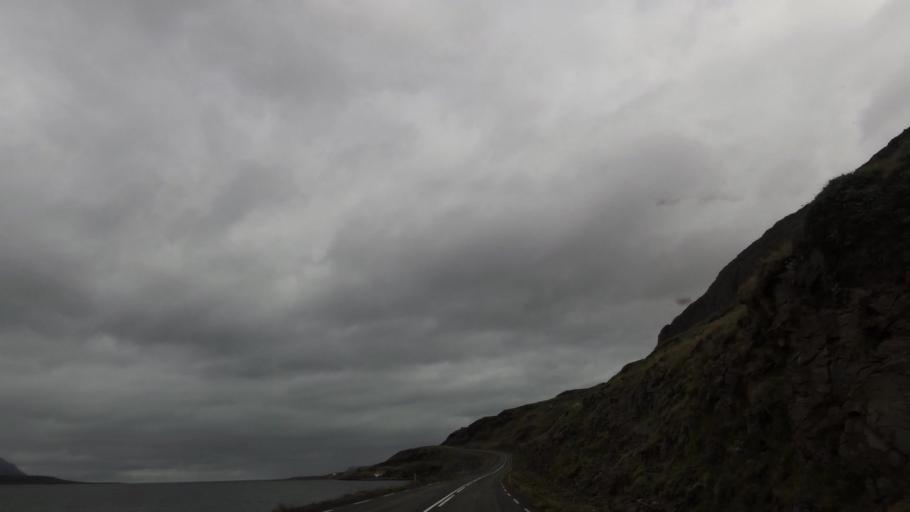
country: IS
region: Westfjords
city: Isafjoerdur
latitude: 65.9924
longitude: -22.7784
